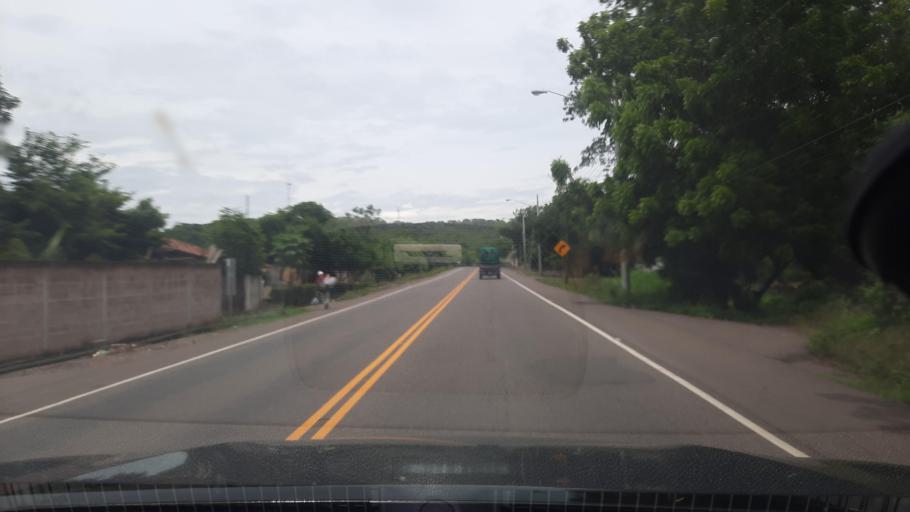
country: HN
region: Valle
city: Goascoran
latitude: 13.5573
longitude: -87.6532
